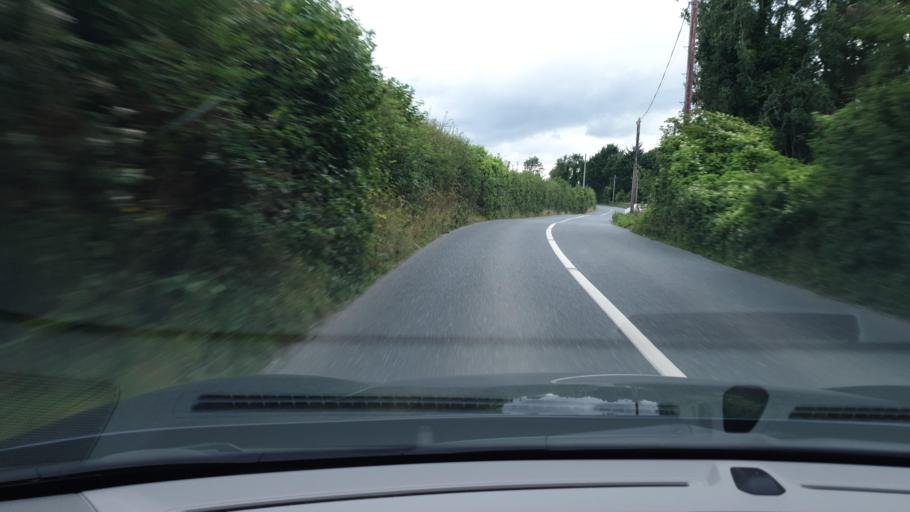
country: IE
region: Leinster
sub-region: South Dublin
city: Saggart
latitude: 53.2743
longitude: -6.4339
